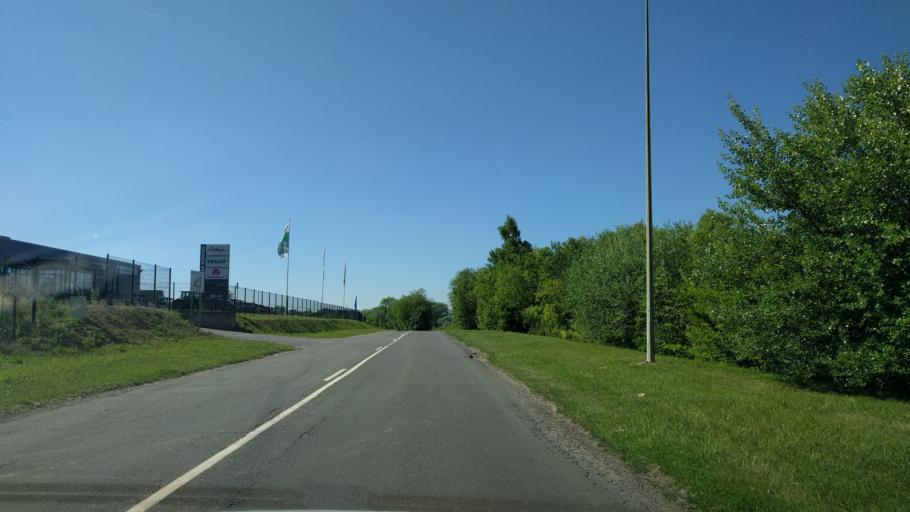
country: FR
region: Picardie
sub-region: Departement de la Somme
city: Peronne
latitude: 49.9162
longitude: 2.9268
